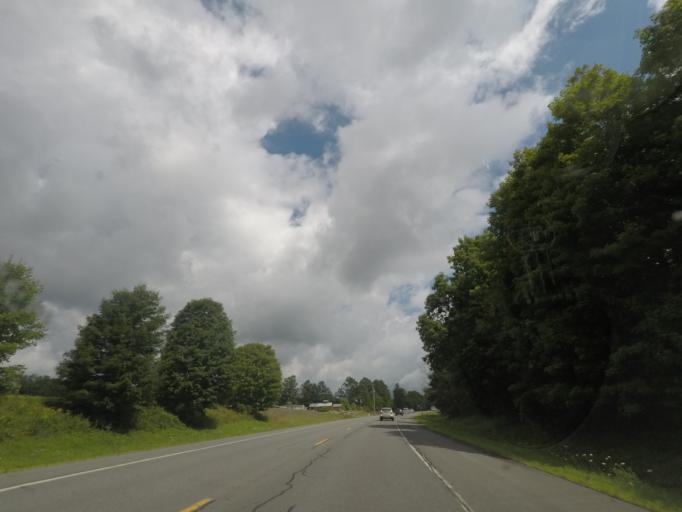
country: US
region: Massachusetts
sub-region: Berkshire County
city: Lanesborough
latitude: 42.5584
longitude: -73.3740
